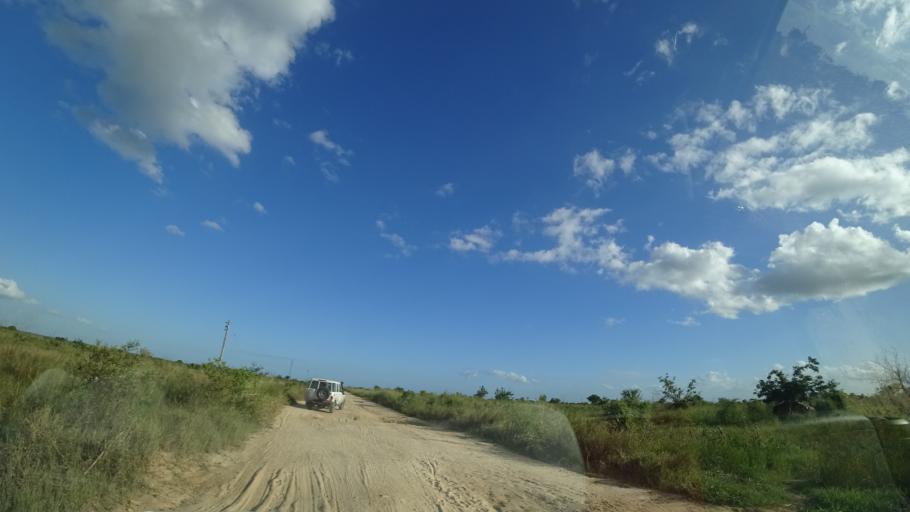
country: MZ
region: Sofala
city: Dondo
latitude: -19.4457
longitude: 34.5621
